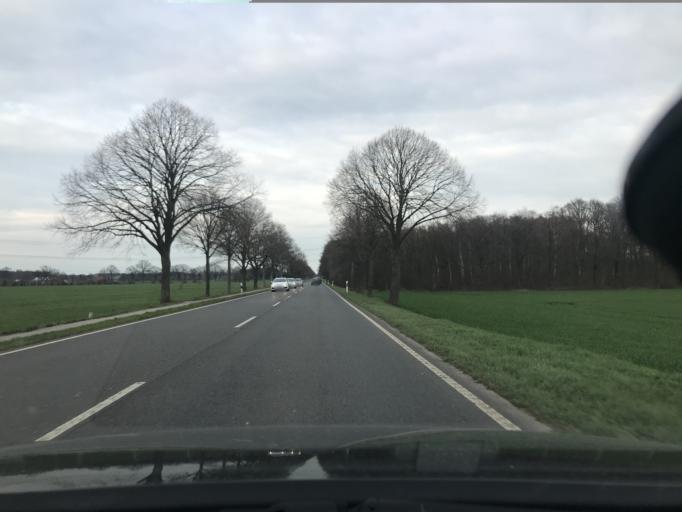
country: DE
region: North Rhine-Westphalia
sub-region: Regierungsbezirk Dusseldorf
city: Wesel
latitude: 51.6877
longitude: 6.6560
